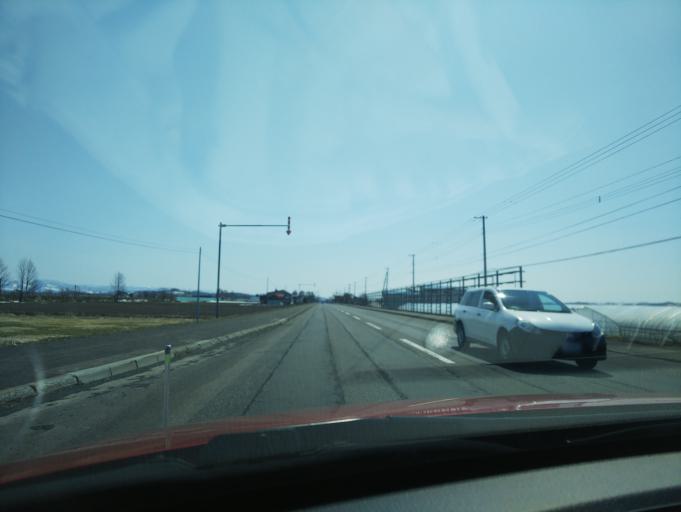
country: JP
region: Hokkaido
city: Nayoro
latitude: 44.2151
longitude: 142.3949
